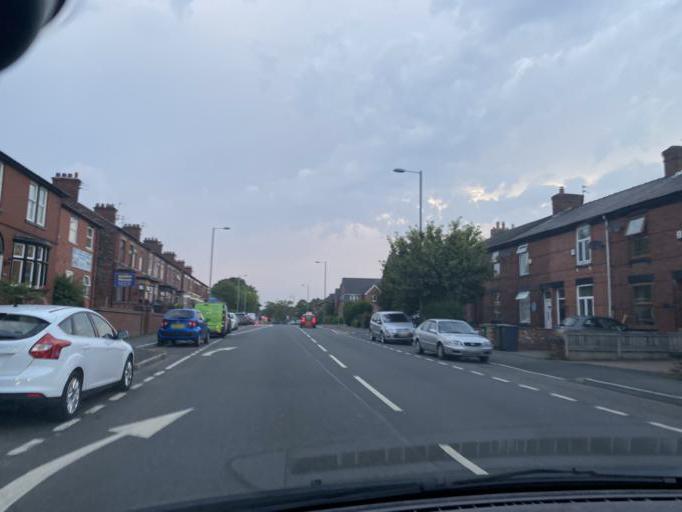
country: GB
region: England
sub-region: Borough of Tameside
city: Droylsden
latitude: 53.4738
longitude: -2.1388
